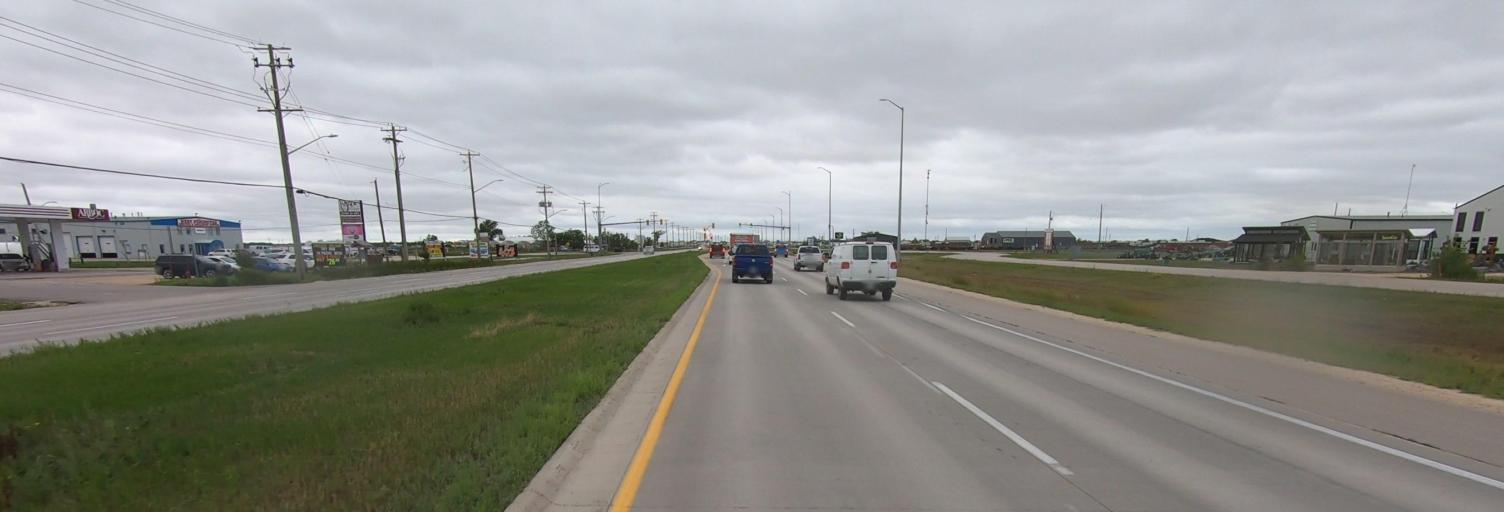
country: CA
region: Manitoba
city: Headingley
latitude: 49.8758
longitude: -97.3741
